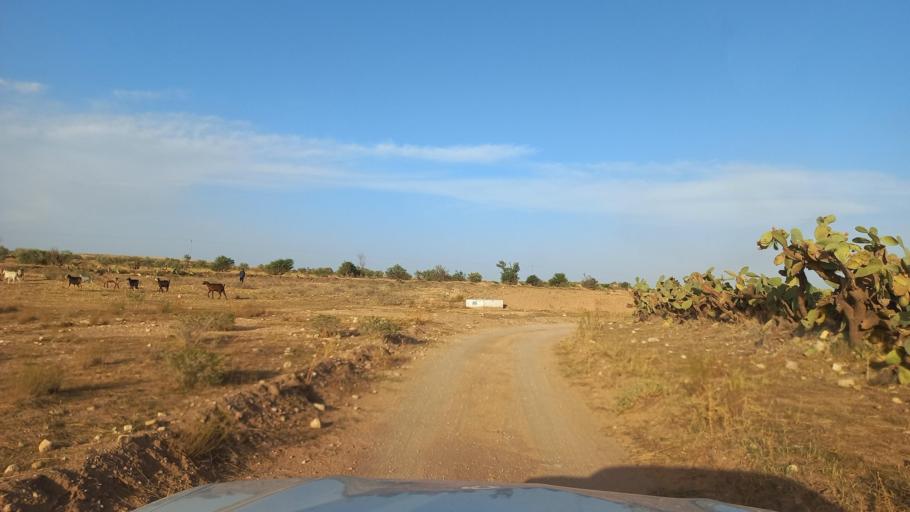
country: TN
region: Al Qasrayn
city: Kasserine
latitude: 35.2571
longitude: 8.9095
